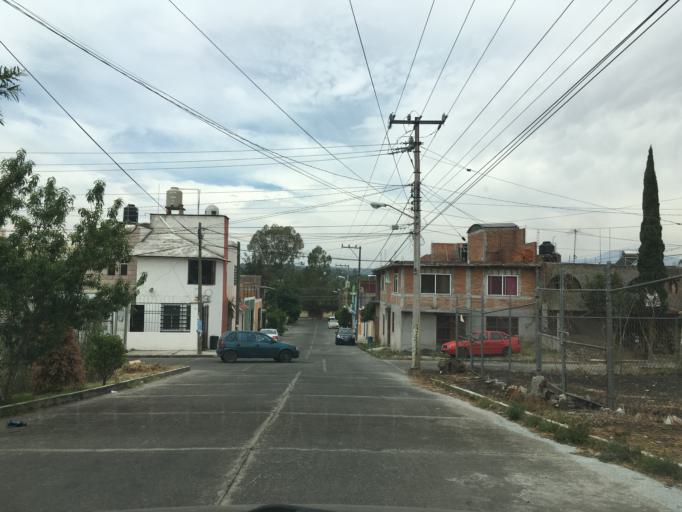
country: MX
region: Michoacan
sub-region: Morelia
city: Morelos
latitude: 19.6699
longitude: -101.2131
